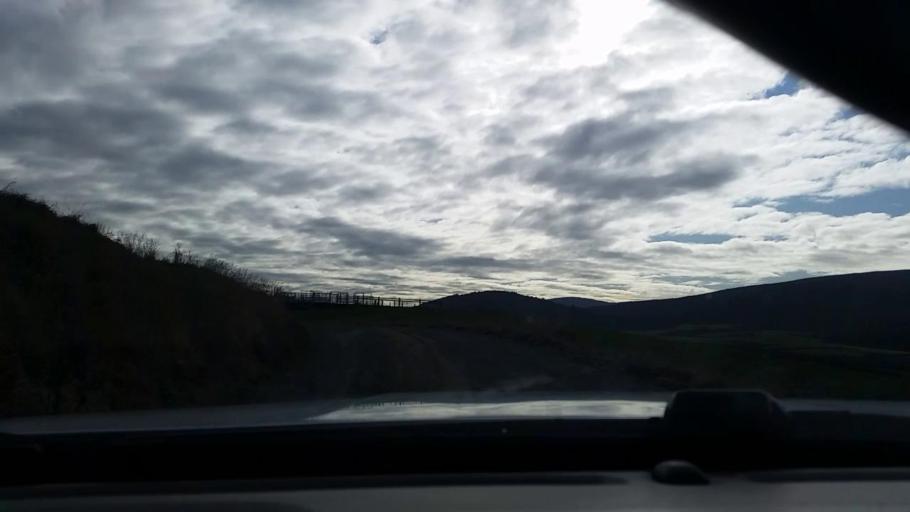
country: NZ
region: Southland
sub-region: Southland District
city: Riverton
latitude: -46.3288
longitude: 167.7991
